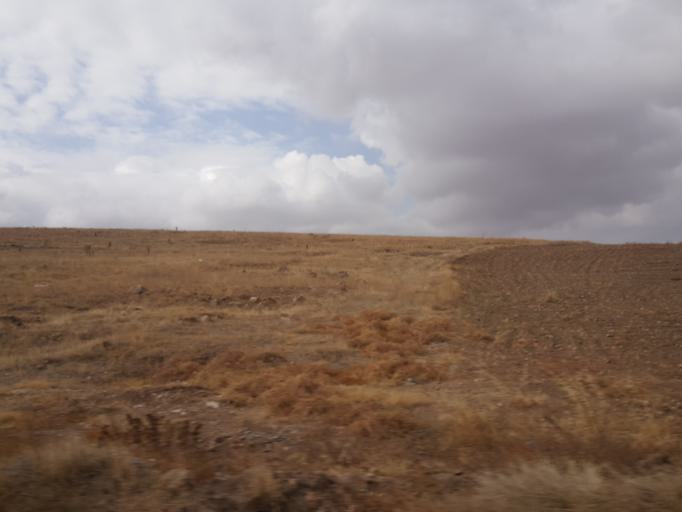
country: TR
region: Kirikkale
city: Keskin
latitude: 39.6503
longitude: 33.6191
